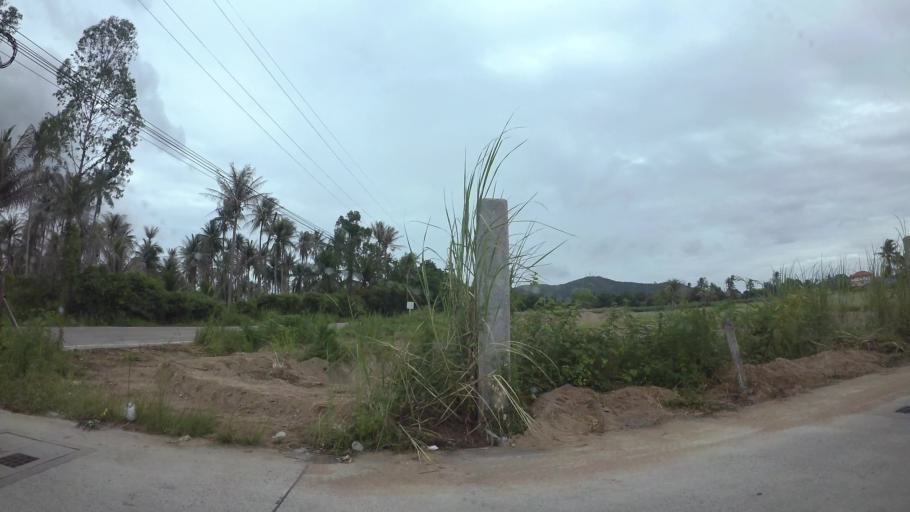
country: TH
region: Chon Buri
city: Si Racha
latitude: 13.1764
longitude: 100.9800
